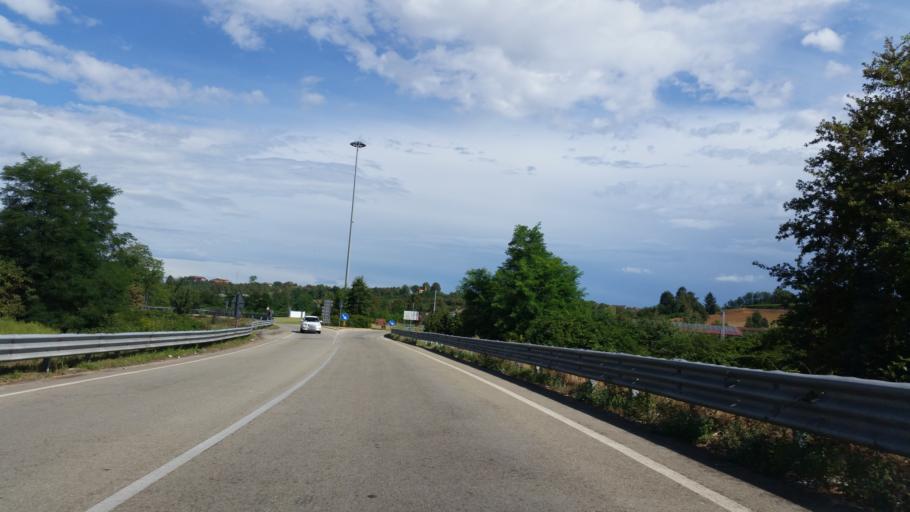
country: IT
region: Piedmont
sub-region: Provincia di Cuneo
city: Monta
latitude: 44.8201
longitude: 7.9482
